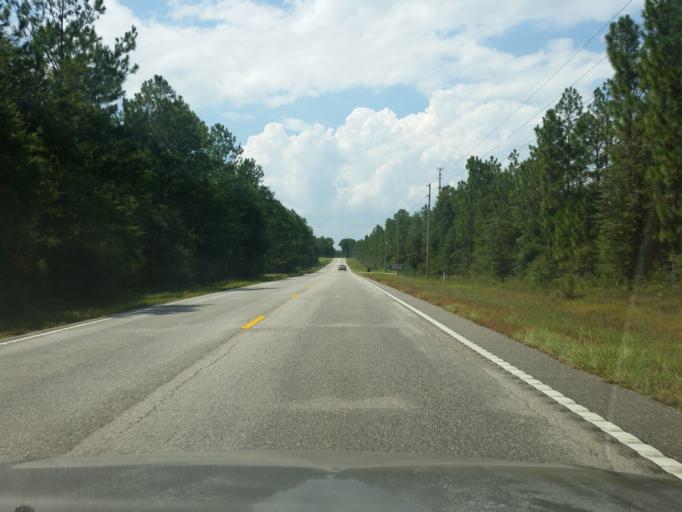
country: US
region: Alabama
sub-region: Baldwin County
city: Elberta
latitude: 30.5180
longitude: -87.4812
